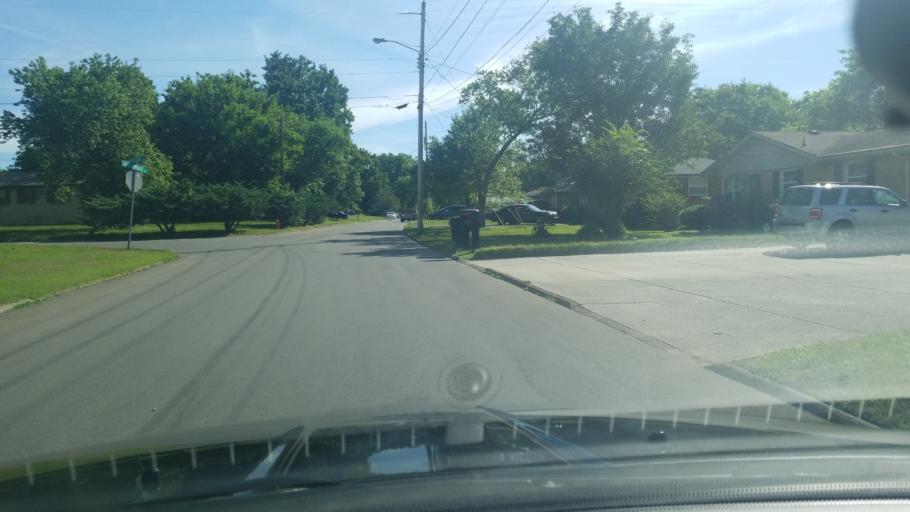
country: US
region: Tennessee
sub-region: Davidson County
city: Nashville
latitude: 36.2373
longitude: -86.7721
